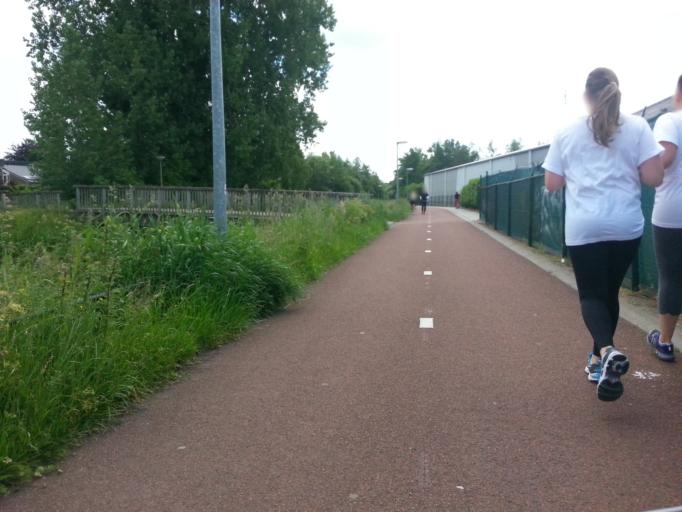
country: NL
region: Gelderland
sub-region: Gemeente Barneveld
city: Barneveld
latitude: 52.1314
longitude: 5.5700
